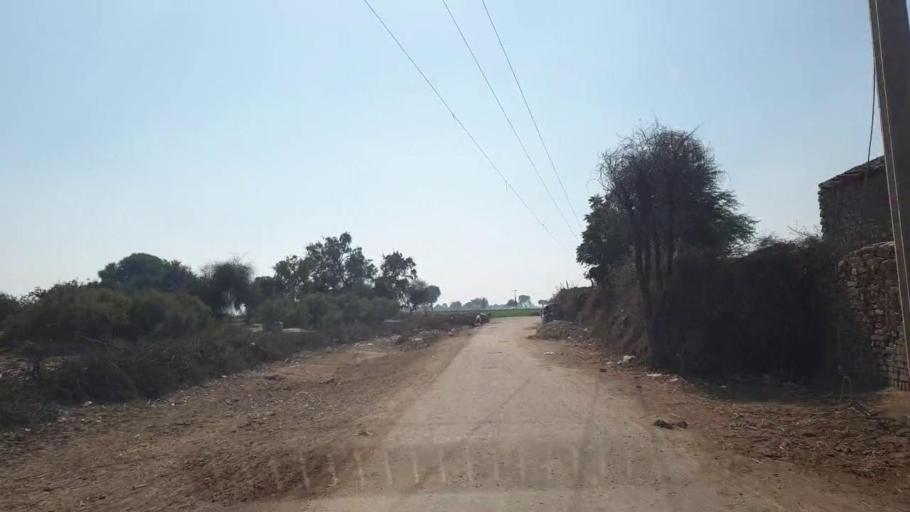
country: PK
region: Sindh
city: Shahpur Chakar
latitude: 26.1027
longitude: 68.6333
